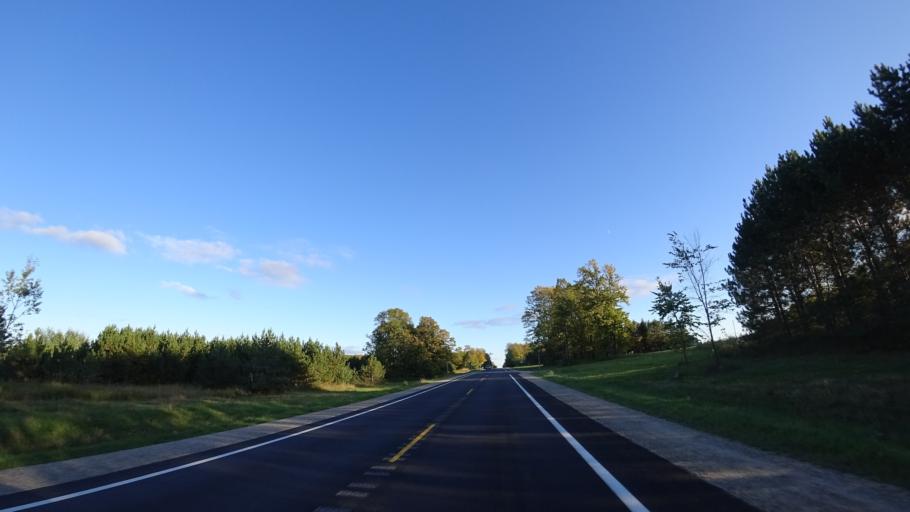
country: US
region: Michigan
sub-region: Luce County
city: Newberry
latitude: 46.3253
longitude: -85.6713
